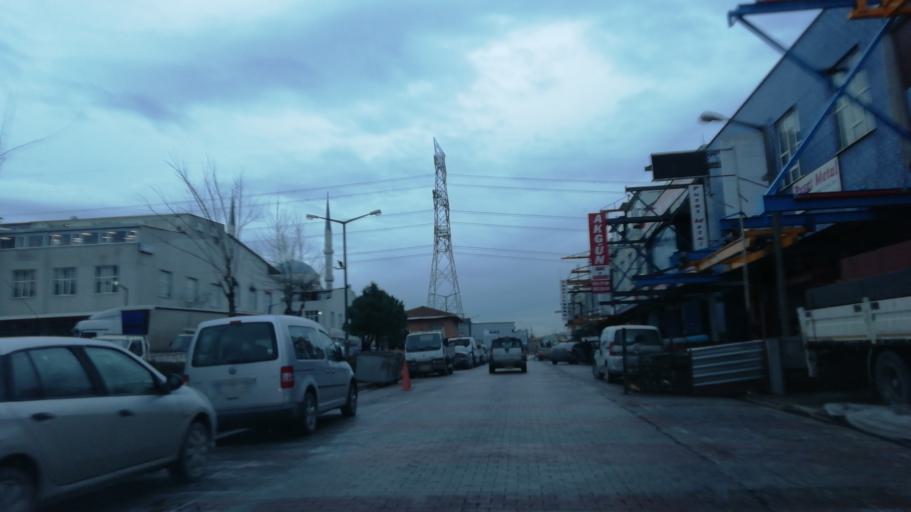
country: TR
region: Istanbul
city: Mahmutbey
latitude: 41.0675
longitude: 28.8065
